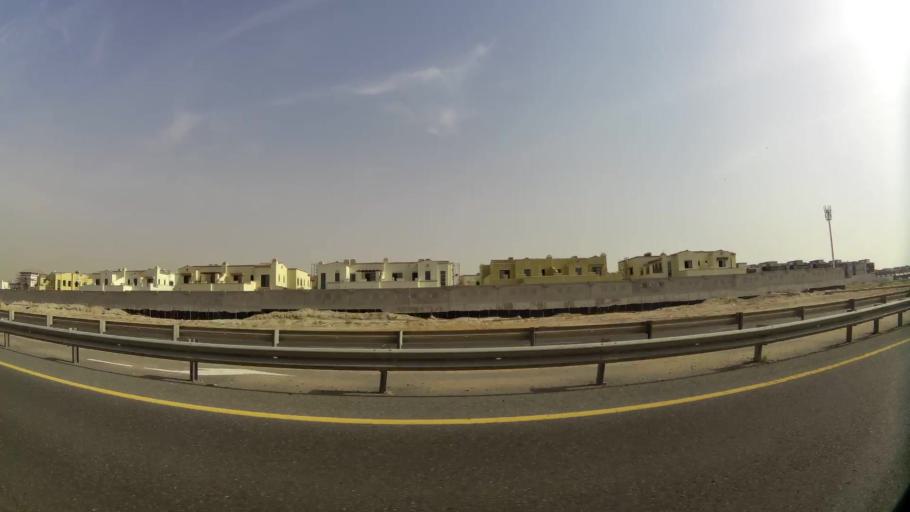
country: AE
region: Ash Shariqah
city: Sharjah
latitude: 25.2330
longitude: 55.4373
